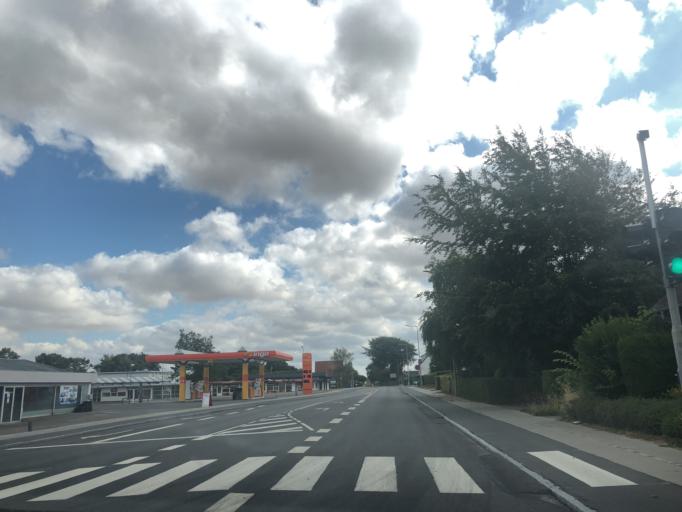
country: DK
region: Central Jutland
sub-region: Struer Kommune
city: Struer
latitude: 56.4801
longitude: 8.6049
